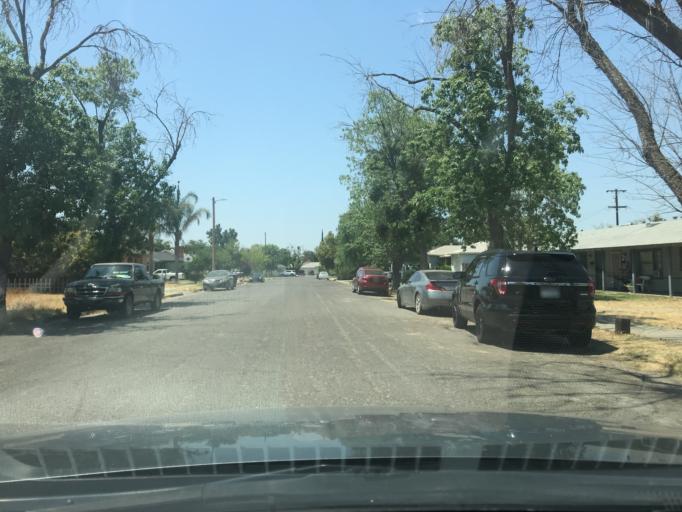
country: US
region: California
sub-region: Merced County
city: Atwater
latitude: 37.3547
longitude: -120.6023
